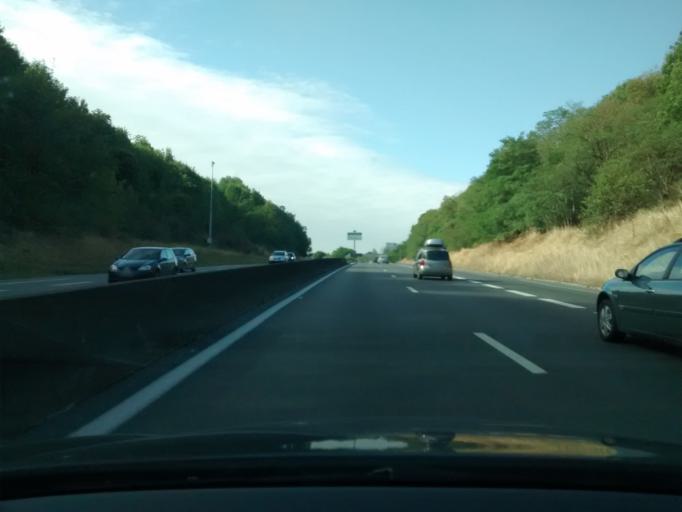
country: FR
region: Ile-de-France
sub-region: Departement de l'Essonne
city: Orsay
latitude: 48.6900
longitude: 2.1917
